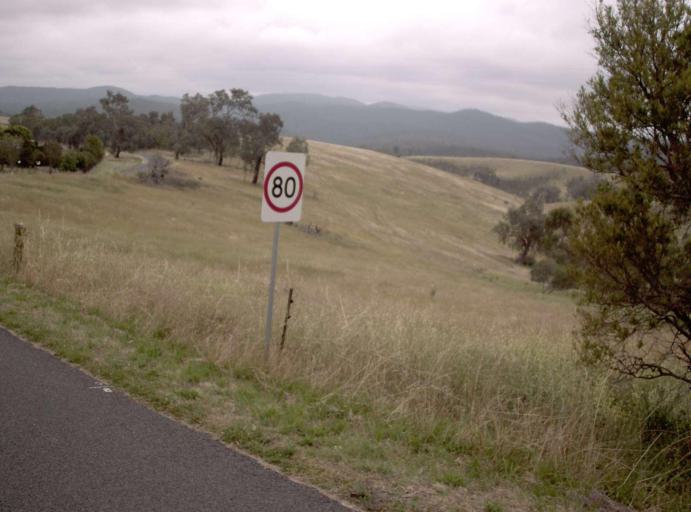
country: AU
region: Victoria
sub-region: Wellington
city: Heyfield
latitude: -37.8685
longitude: 146.7064
